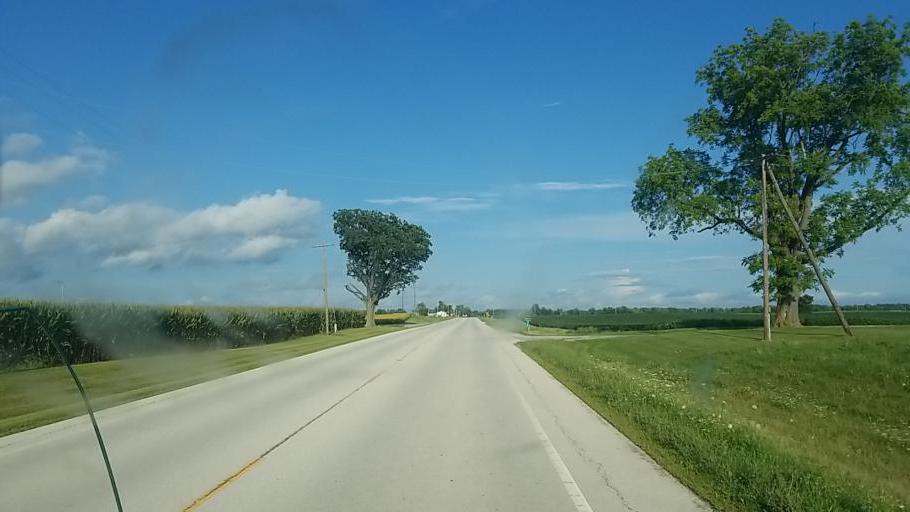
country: US
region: Ohio
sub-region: Wyandot County
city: Upper Sandusky
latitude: 40.8407
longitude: -83.1393
